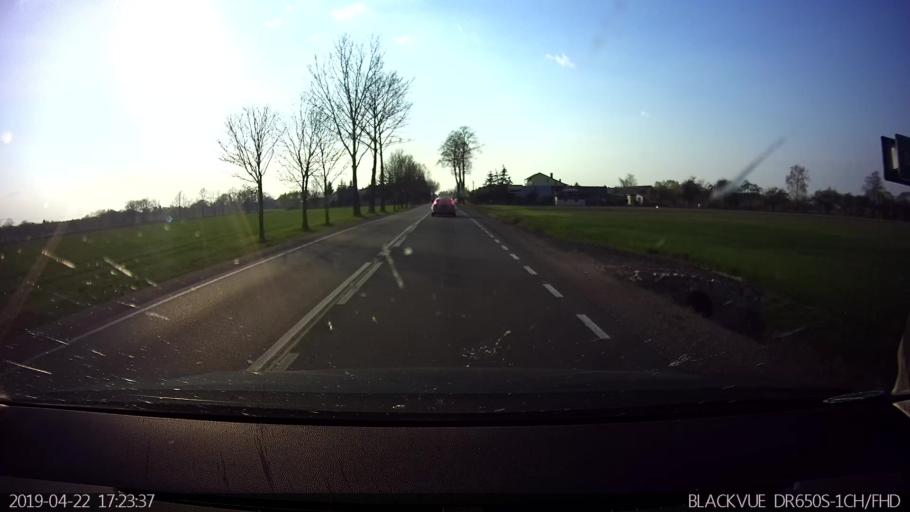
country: PL
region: Masovian Voivodeship
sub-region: Powiat sokolowski
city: Sokolow Podlaski
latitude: 52.3922
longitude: 22.3142
